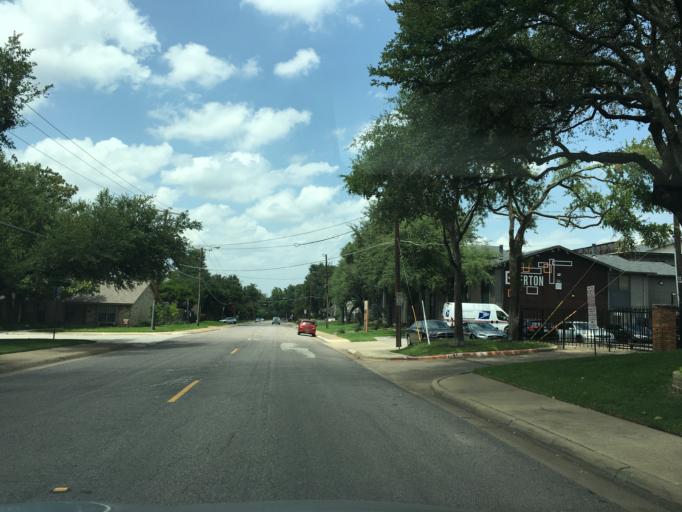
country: US
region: Texas
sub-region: Dallas County
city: University Park
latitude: 32.8904
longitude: -96.7750
